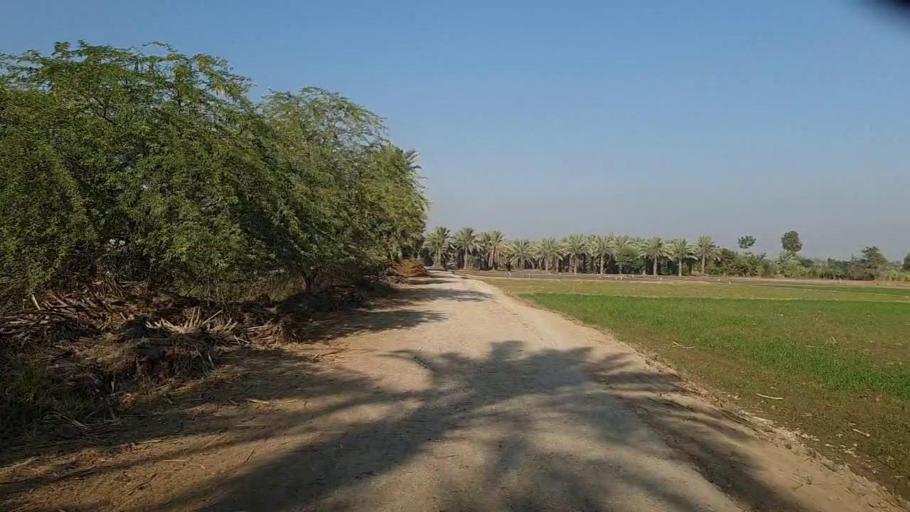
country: PK
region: Sindh
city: Ranipur
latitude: 27.2559
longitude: 68.5523
